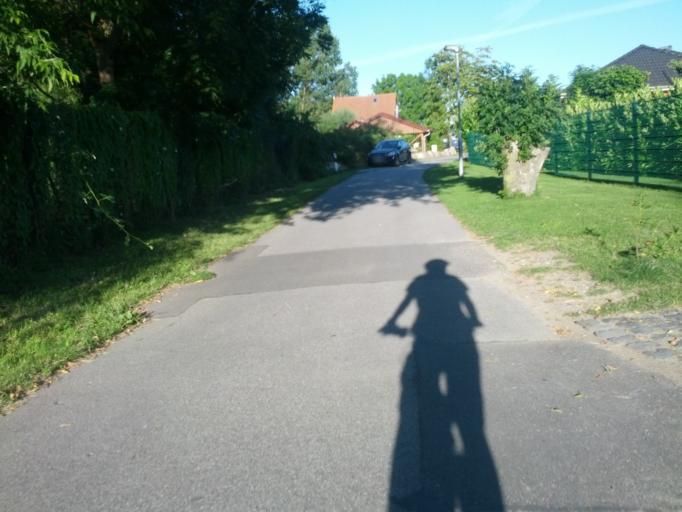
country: DE
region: Mecklenburg-Vorpommern
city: Bastorf
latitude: 54.1133
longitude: 11.6351
